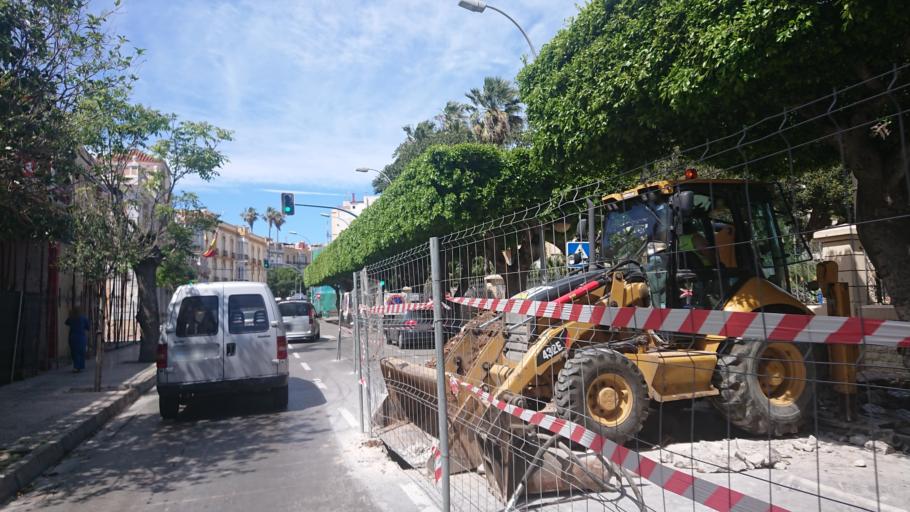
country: ES
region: Melilla
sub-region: Melilla
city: Melilla
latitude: 35.2918
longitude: -2.9427
